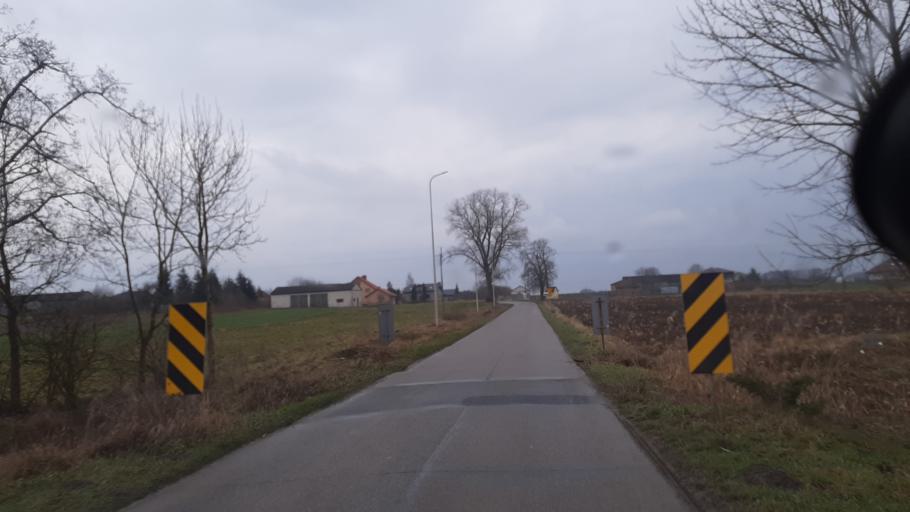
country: PL
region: Lublin Voivodeship
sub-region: Powiat lubelski
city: Jastkow
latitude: 51.3623
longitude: 22.4553
